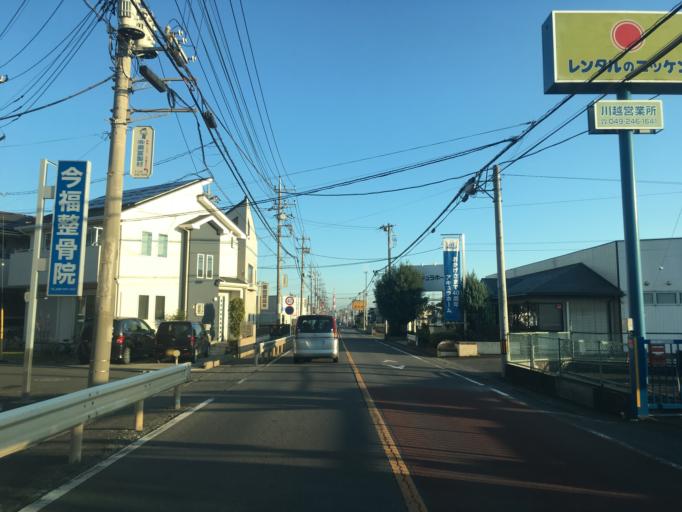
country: JP
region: Saitama
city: Kawagoe
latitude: 35.8822
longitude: 139.4758
